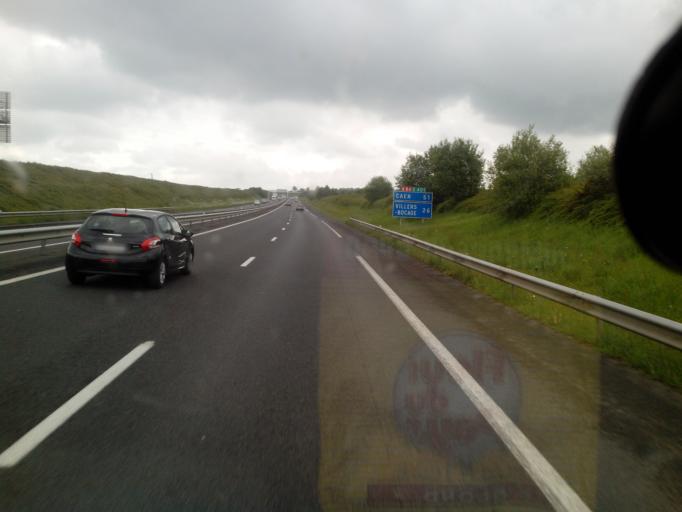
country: FR
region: Lower Normandy
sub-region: Departement de la Manche
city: Saint-Amand
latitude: 48.9858
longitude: -0.9346
